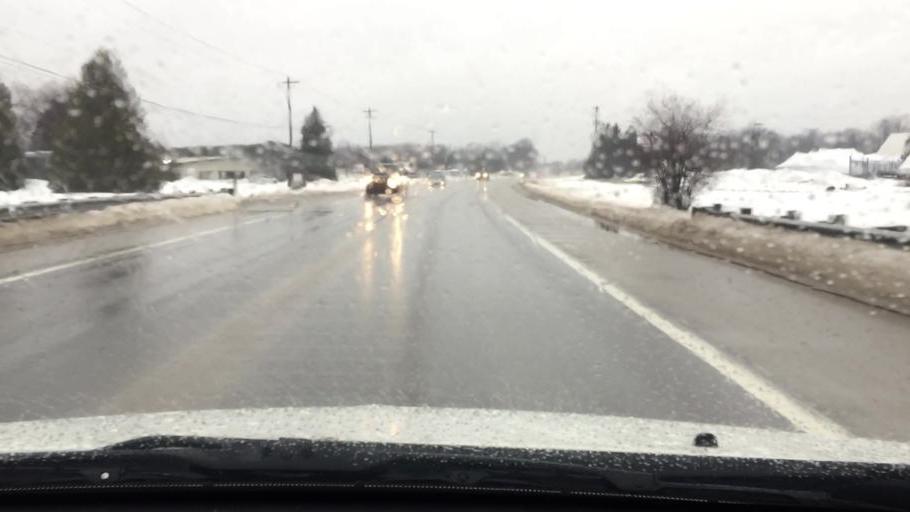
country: US
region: Michigan
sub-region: Charlevoix County
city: Charlevoix
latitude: 45.2959
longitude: -85.2538
